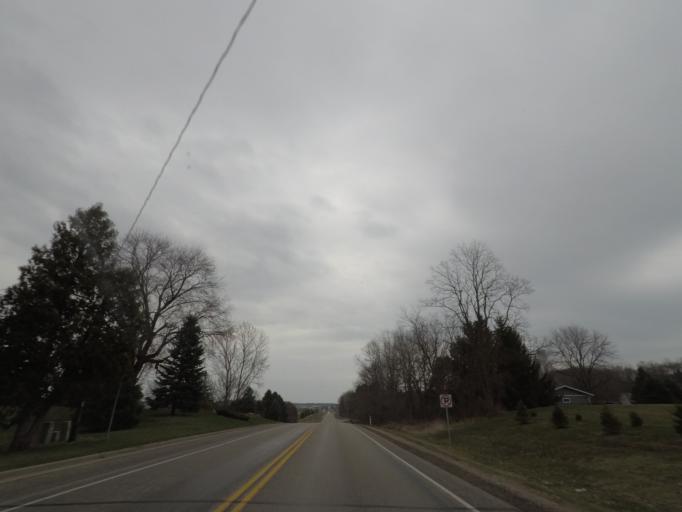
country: US
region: Wisconsin
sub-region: Dane County
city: Middleton
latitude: 43.1111
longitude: -89.5486
